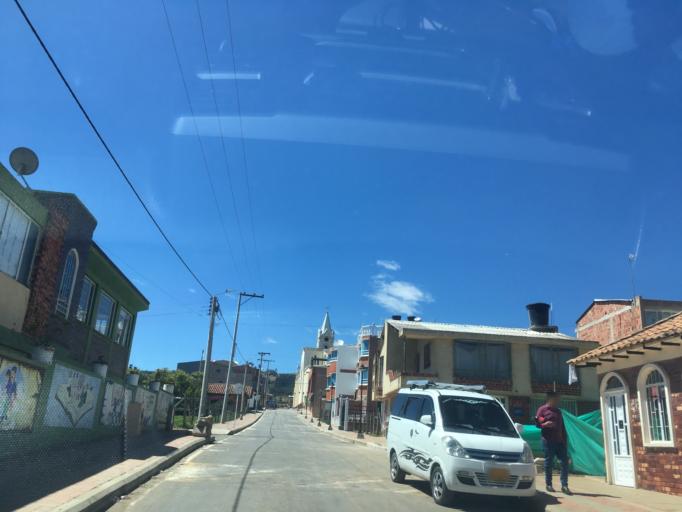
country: CO
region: Boyaca
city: Combita
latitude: 5.6337
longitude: -73.3221
